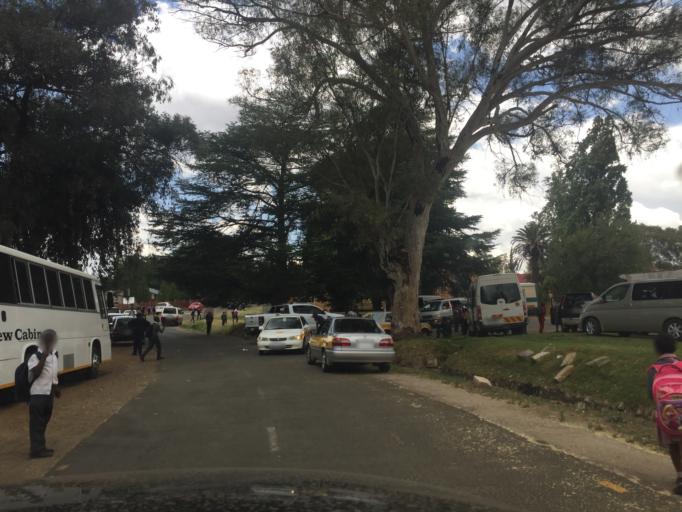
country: LS
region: Maseru
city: Nako
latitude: -29.4485
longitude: 27.7229
